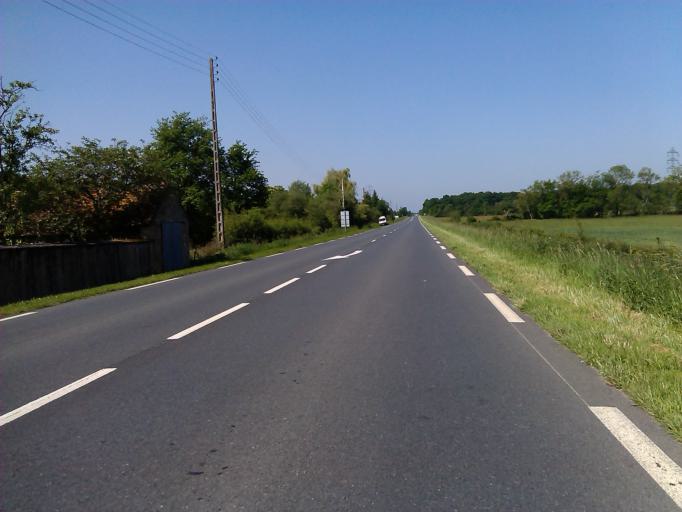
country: FR
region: Centre
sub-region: Departement de l'Indre
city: Arthon
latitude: 46.6147
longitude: 1.6807
